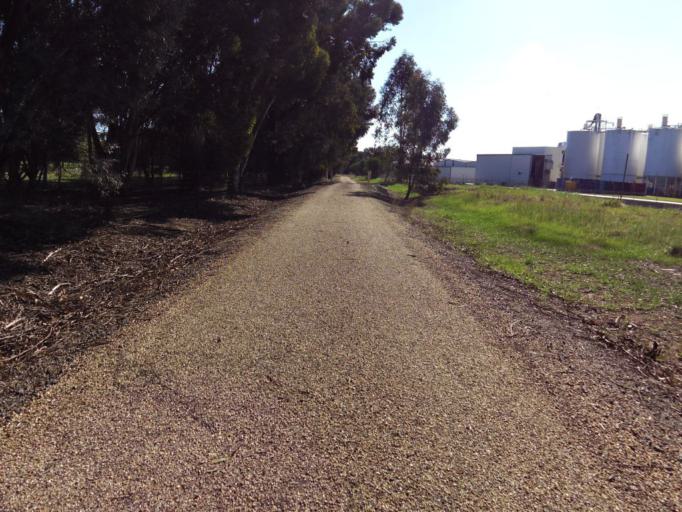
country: AU
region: New South Wales
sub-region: Corowa Shire
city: Corowa
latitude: -36.0136
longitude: 146.4094
